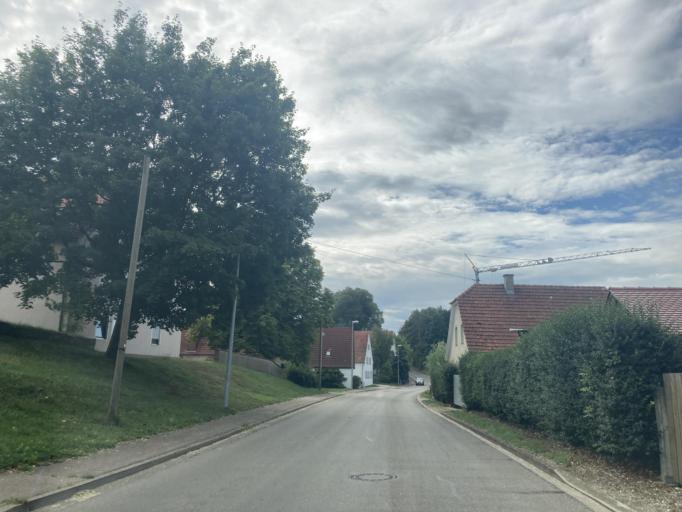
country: DE
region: Bavaria
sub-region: Swabia
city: Mottingen
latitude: 48.8138
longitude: 10.6035
